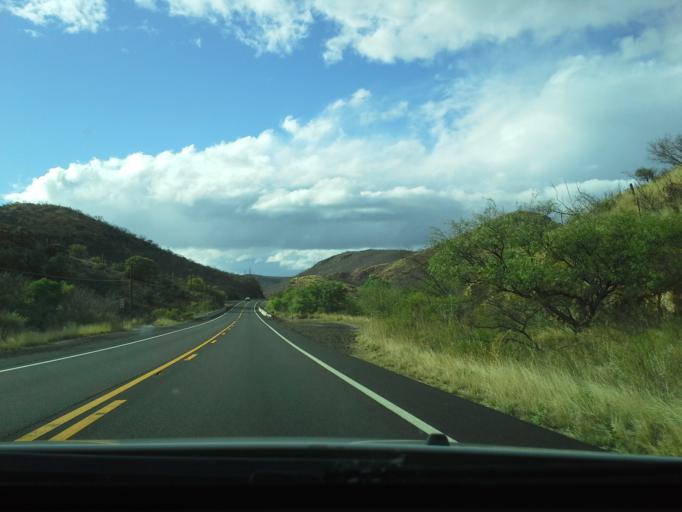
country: US
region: Arizona
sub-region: Cochise County
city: Bisbee
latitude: 31.5009
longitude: -110.0041
